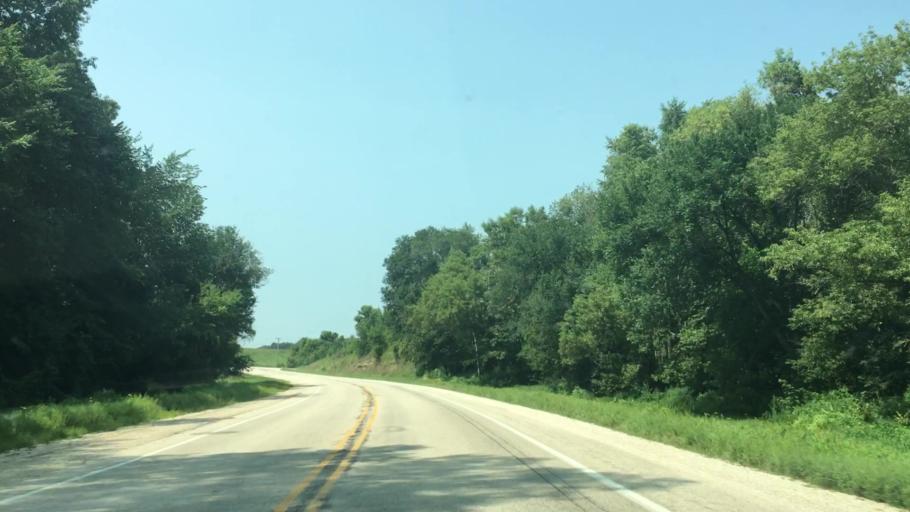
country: US
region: Iowa
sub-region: Fayette County
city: West Union
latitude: 43.0782
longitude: -91.8402
